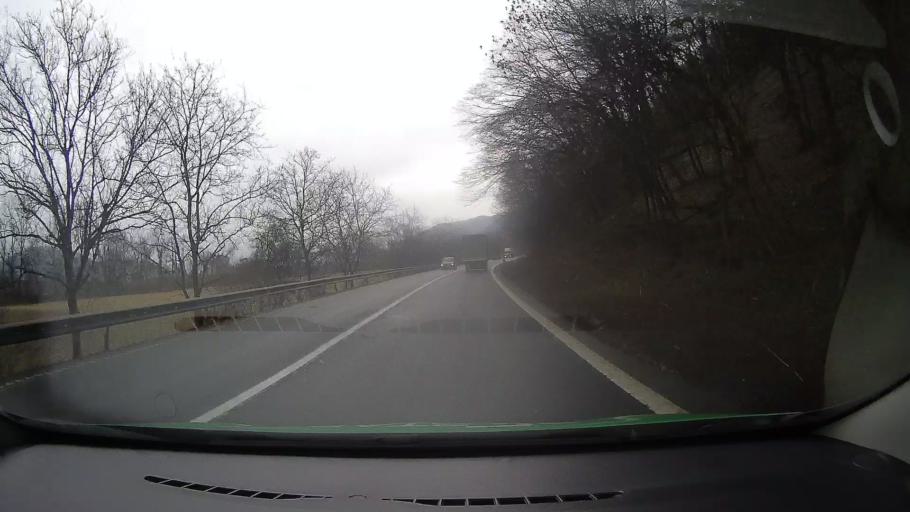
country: RO
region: Hunedoara
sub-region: Comuna Branisca
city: Branisca
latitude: 45.9135
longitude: 22.7662
